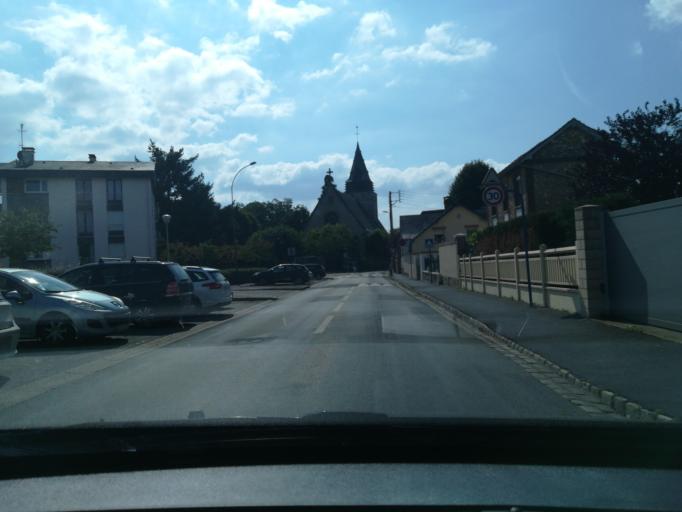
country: FR
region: Haute-Normandie
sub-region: Departement de la Seine-Maritime
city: Bois-Guillaume
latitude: 49.4681
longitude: 1.1106
